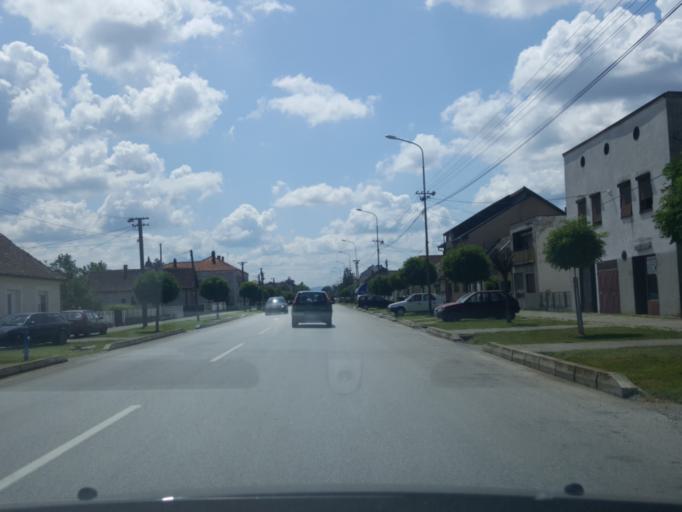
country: RS
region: Central Serbia
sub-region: Macvanski Okrug
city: Bogatic
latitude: 44.8407
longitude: 19.4812
